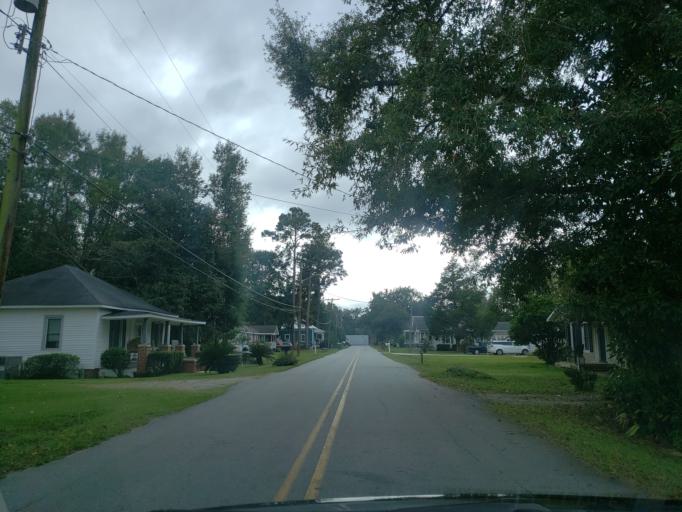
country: US
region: Georgia
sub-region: Chatham County
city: Pooler
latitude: 32.1176
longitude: -81.2463
